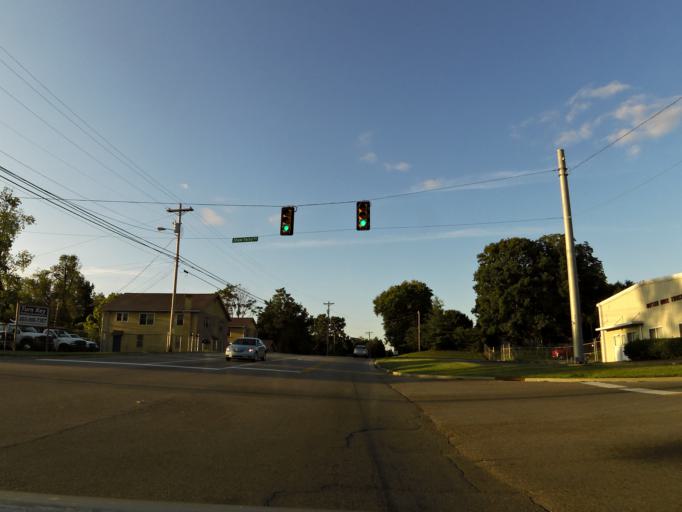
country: US
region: Tennessee
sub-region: Loudon County
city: Lenoir City
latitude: 35.8230
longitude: -84.2529
